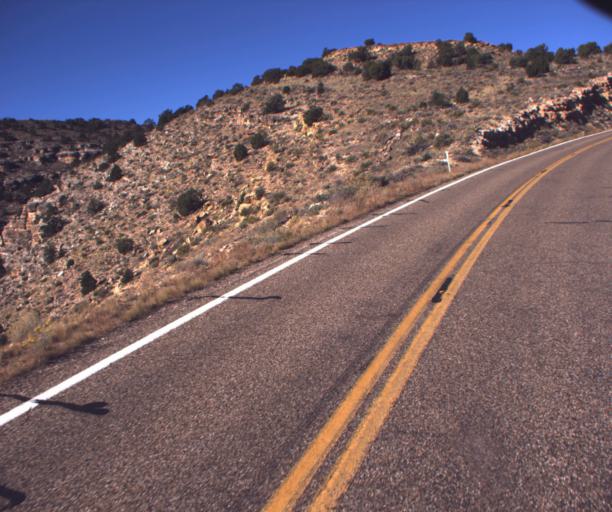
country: US
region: Arizona
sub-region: Coconino County
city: Fredonia
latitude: 36.7227
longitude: -112.0623
